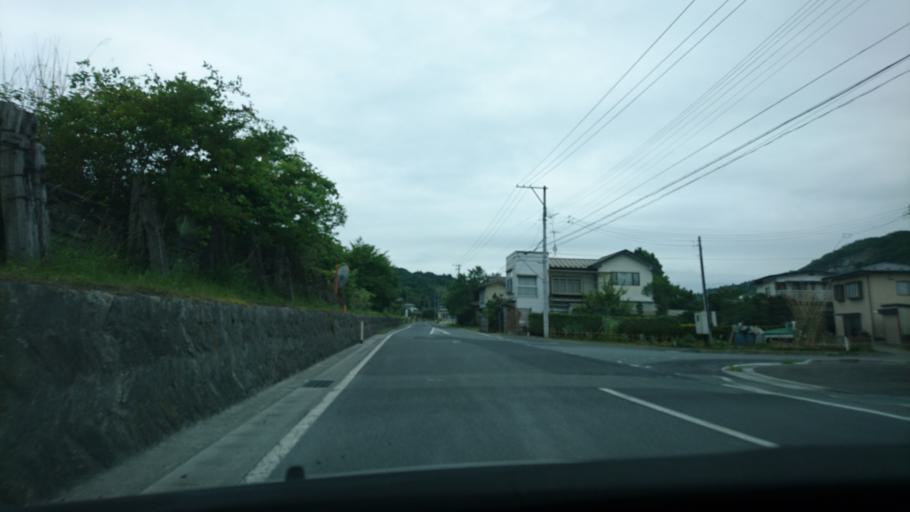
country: JP
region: Iwate
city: Ichinoseki
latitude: 38.9777
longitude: 141.2393
